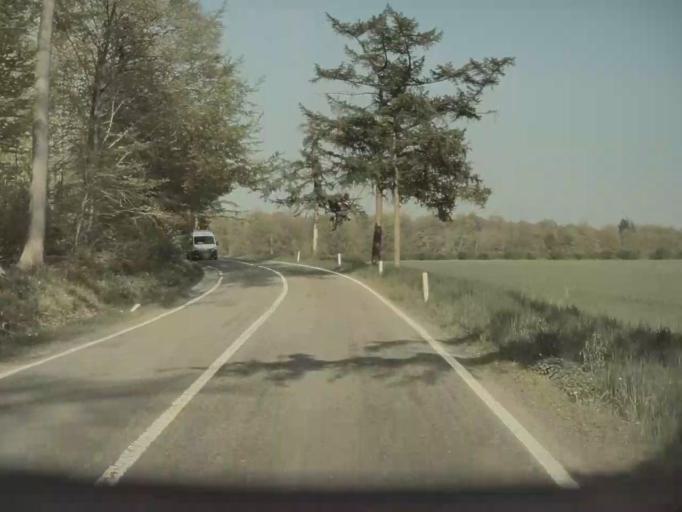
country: BE
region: Wallonia
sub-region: Province de Namur
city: Hamois
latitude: 50.2927
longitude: 5.2046
